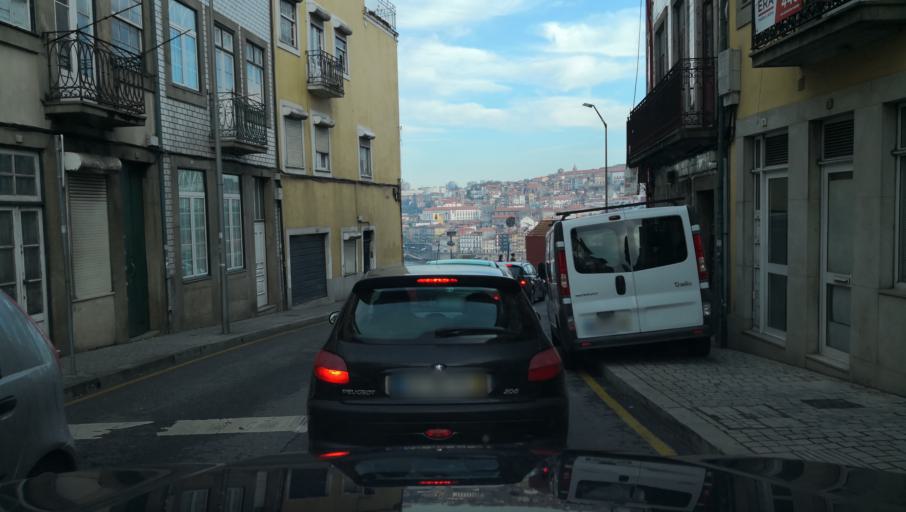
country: PT
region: Porto
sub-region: Vila Nova de Gaia
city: Vila Nova de Gaia
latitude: 41.1351
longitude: -8.6113
